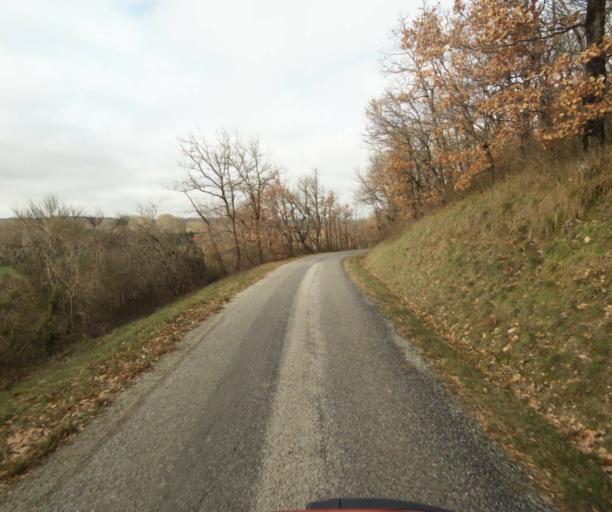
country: FR
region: Languedoc-Roussillon
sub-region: Departement de l'Aude
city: Belpech
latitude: 43.1662
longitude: 1.7379
